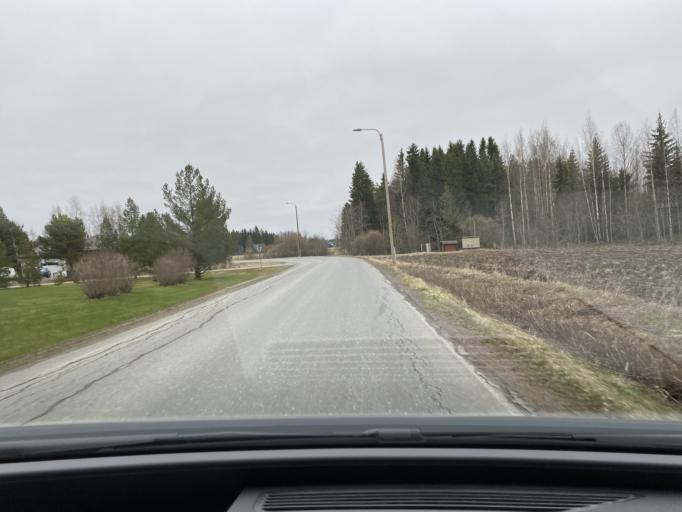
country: FI
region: Satakunta
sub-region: Pori
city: Huittinen
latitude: 61.1648
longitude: 22.7252
